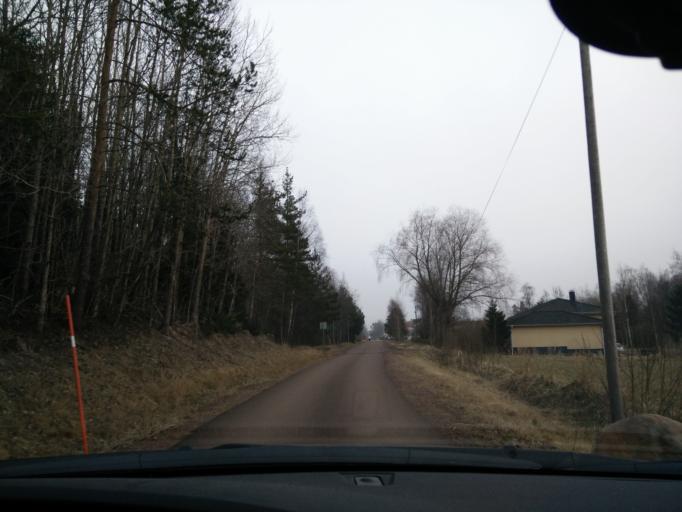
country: AX
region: Mariehamns stad
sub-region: Mariehamn
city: Mariehamn
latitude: 60.1253
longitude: 19.9231
